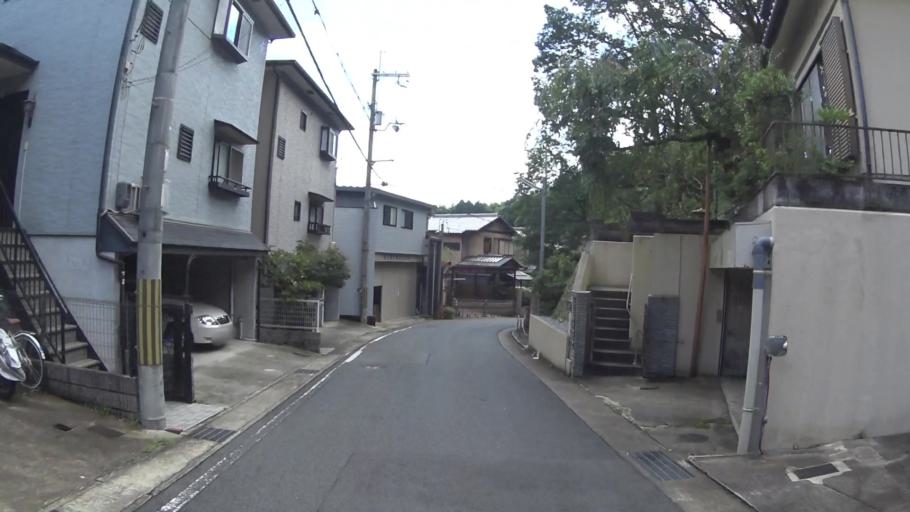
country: JP
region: Kyoto
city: Kyoto
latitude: 34.9739
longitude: 135.7913
